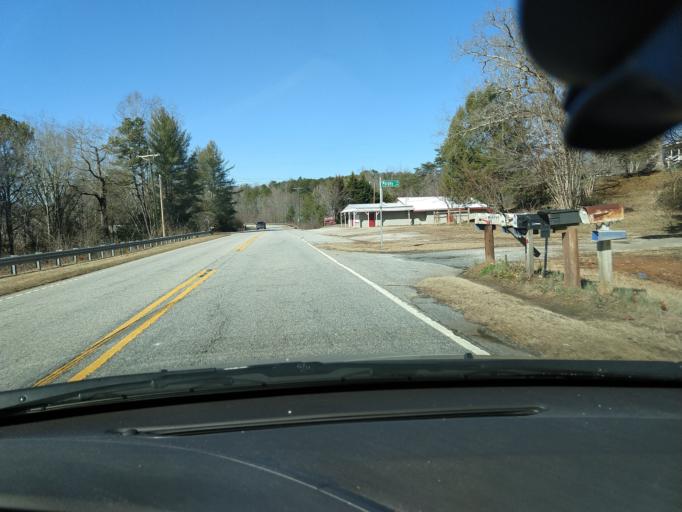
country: US
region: South Carolina
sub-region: Oconee County
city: Westminster
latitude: 34.6153
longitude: -83.1638
